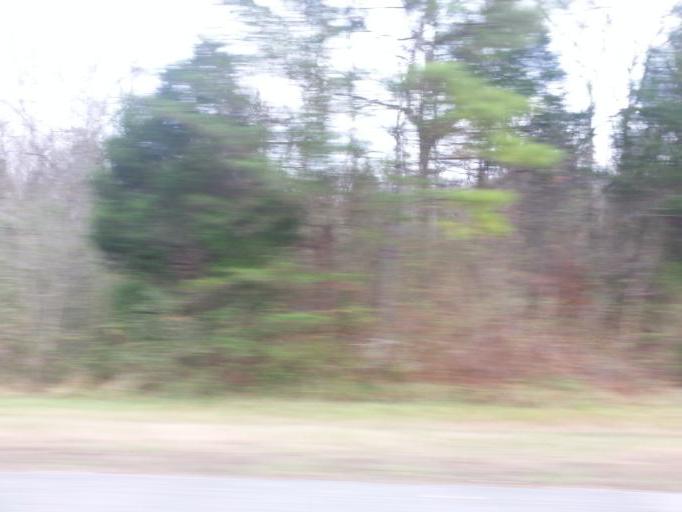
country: US
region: Tennessee
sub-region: Rhea County
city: Graysville
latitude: 35.4279
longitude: -85.0852
